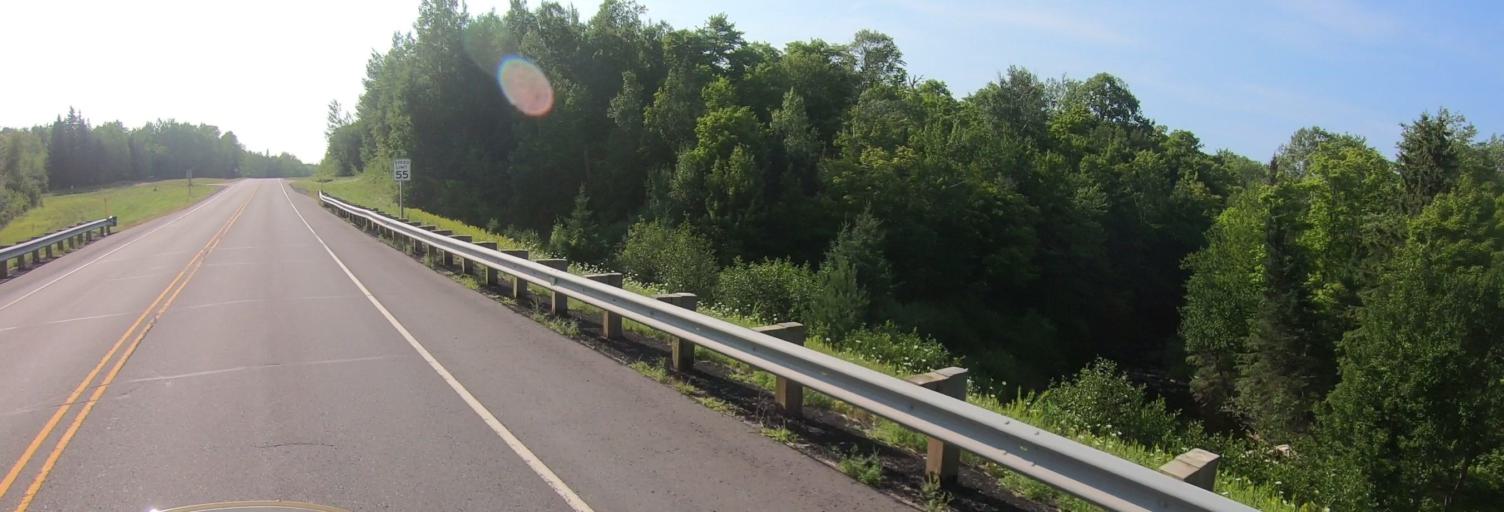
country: US
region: Wisconsin
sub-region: Iron County
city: Hurley
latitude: 46.3667
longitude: -90.4106
